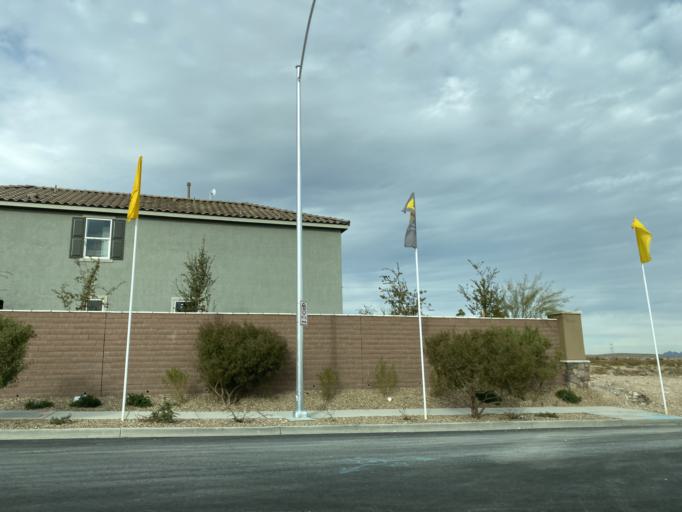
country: US
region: Nevada
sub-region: Clark County
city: Enterprise
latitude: 35.9982
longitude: -115.2733
